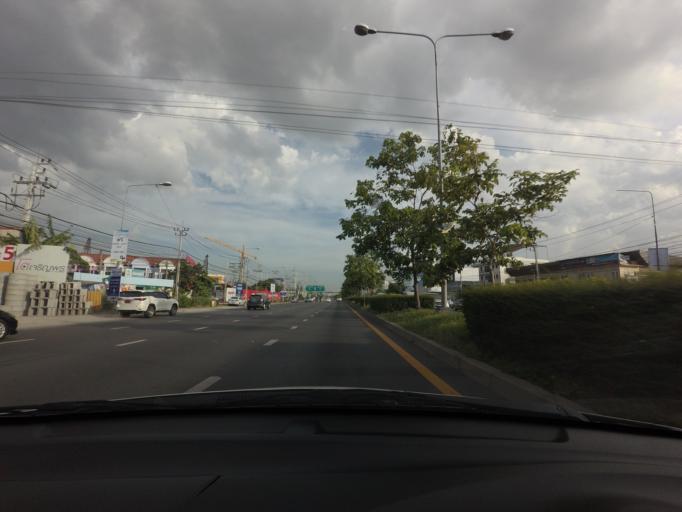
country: TH
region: Nonthaburi
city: Bang Bua Thong
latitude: 13.8834
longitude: 100.4506
